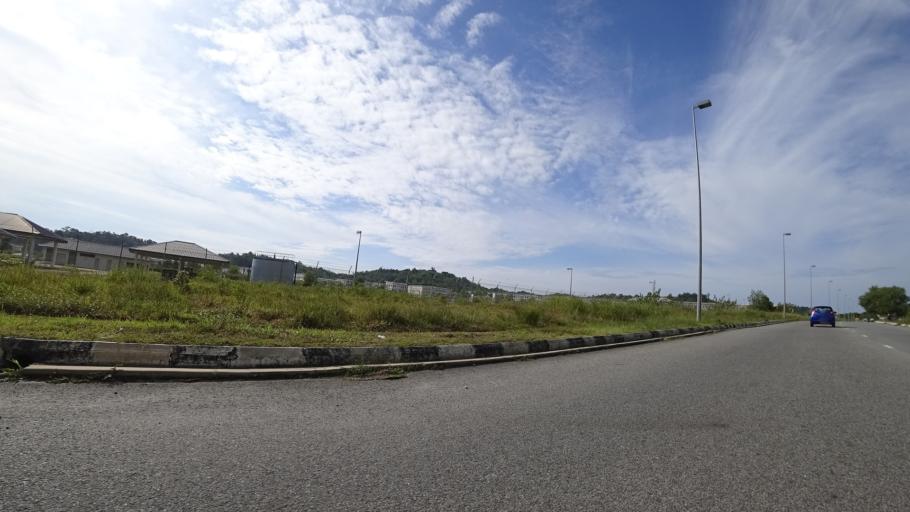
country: BN
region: Brunei and Muara
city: Bandar Seri Begawan
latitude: 4.8882
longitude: 114.8030
